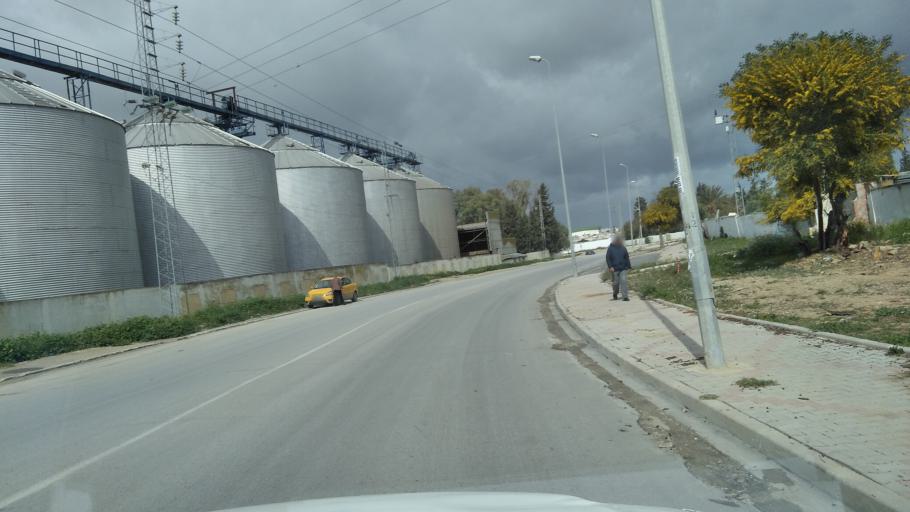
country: TN
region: Bin 'Arus
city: Ben Arous
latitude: 36.7430
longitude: 10.2293
